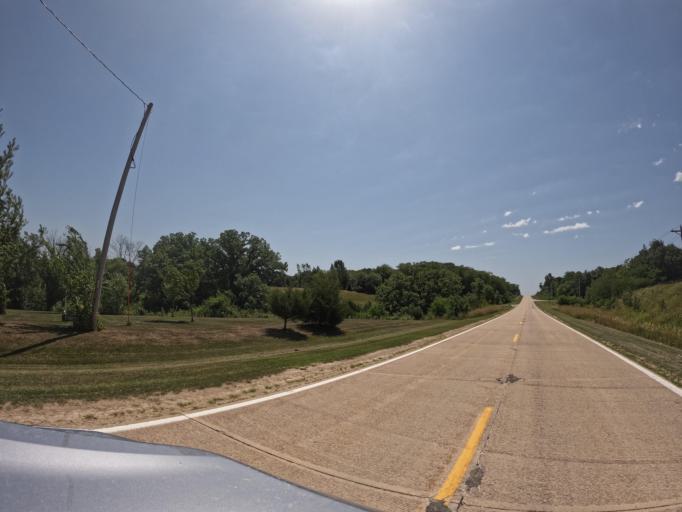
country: US
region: Iowa
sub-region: Henry County
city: Mount Pleasant
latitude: 40.9176
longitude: -91.5542
